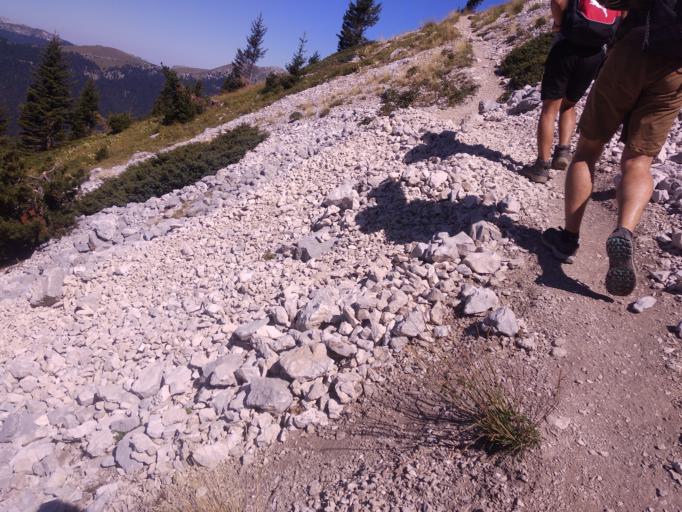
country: FR
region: Rhone-Alpes
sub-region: Departement de l'Isere
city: Le Sappey-en-Chartreuse
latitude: 45.2866
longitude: 5.7814
